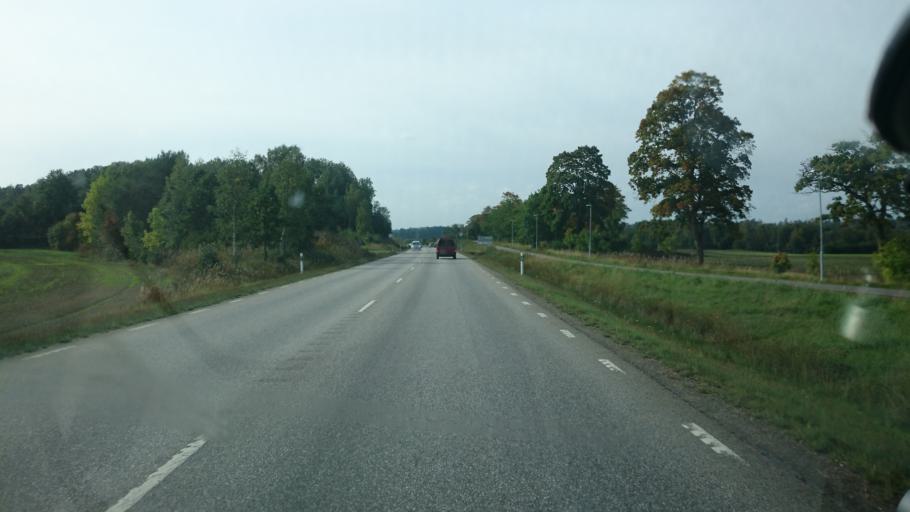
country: SE
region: Vaestra Goetaland
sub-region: Alingsas Kommun
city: Sollebrunn
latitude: 58.1042
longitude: 12.5147
